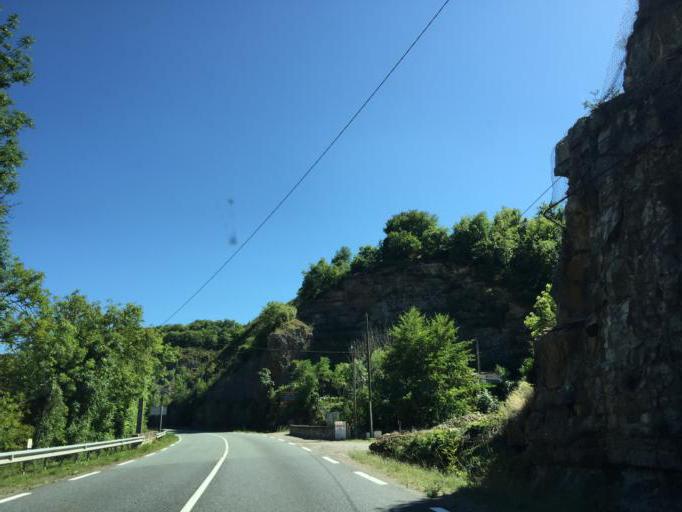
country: FR
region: Midi-Pyrenees
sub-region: Departement de l'Aveyron
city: Saint-Georges-de-Luzencon
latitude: 44.0058
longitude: 2.9640
